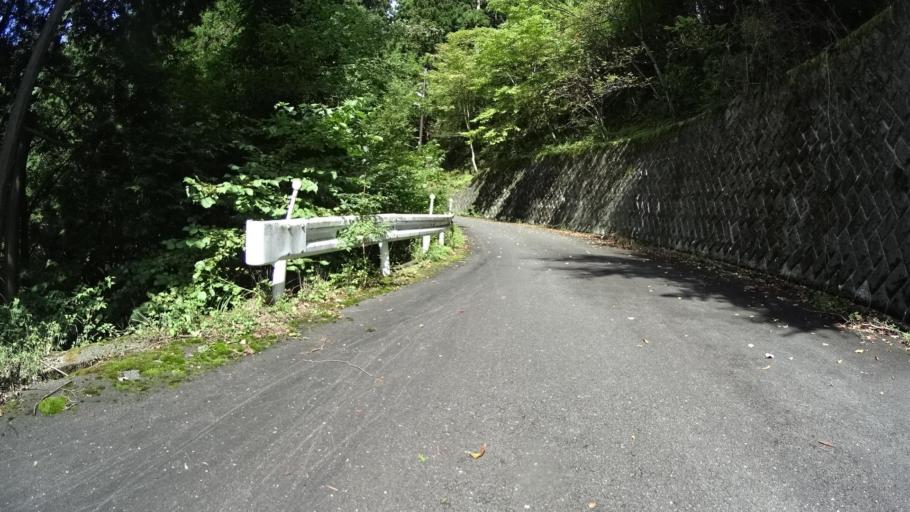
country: JP
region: Yamanashi
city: Uenohara
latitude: 35.7464
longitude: 139.0438
